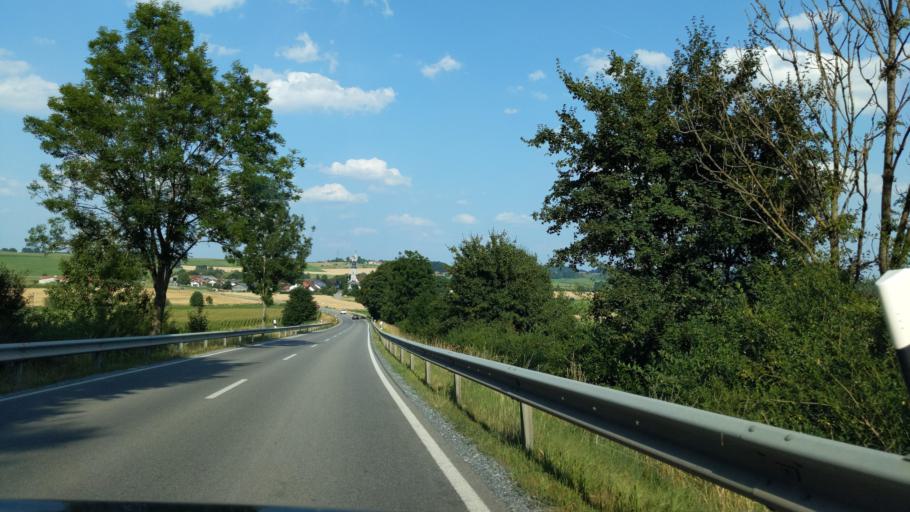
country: DE
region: Bavaria
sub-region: Upper Bavaria
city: Bruck
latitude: 48.0191
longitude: 11.8980
